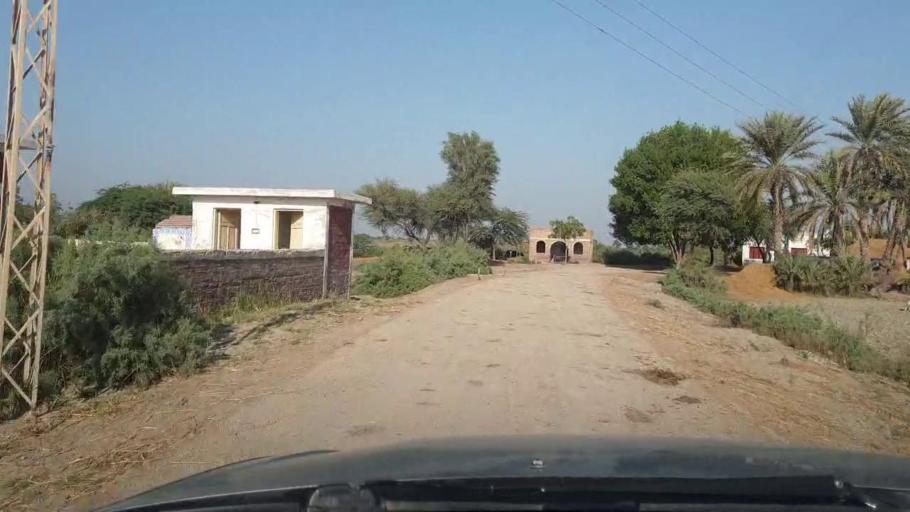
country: PK
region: Sindh
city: Tando Muhammad Khan
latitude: 25.1071
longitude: 68.5632
